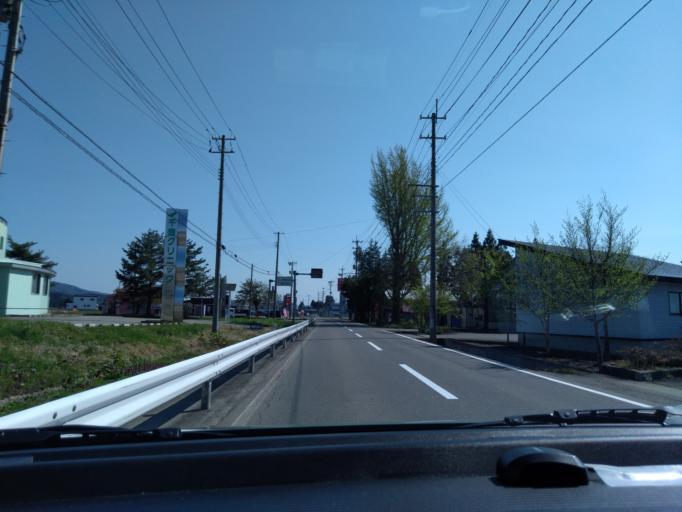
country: JP
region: Akita
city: Omagari
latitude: 39.4613
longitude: 140.5804
